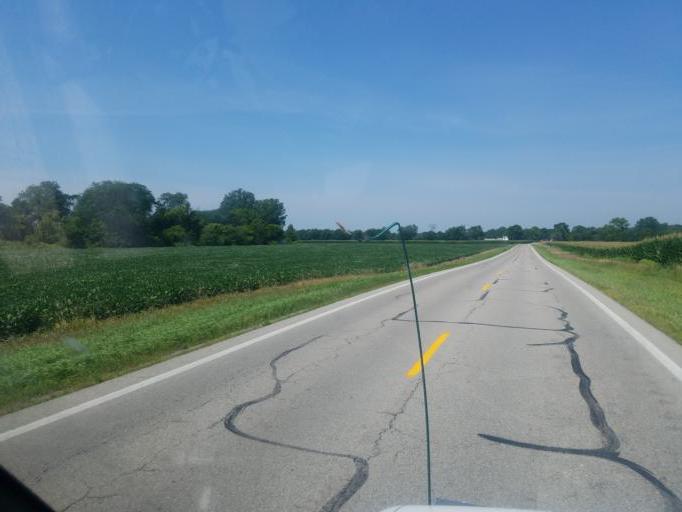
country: US
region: Ohio
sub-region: Logan County
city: West Liberty
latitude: 40.2512
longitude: -83.7400
